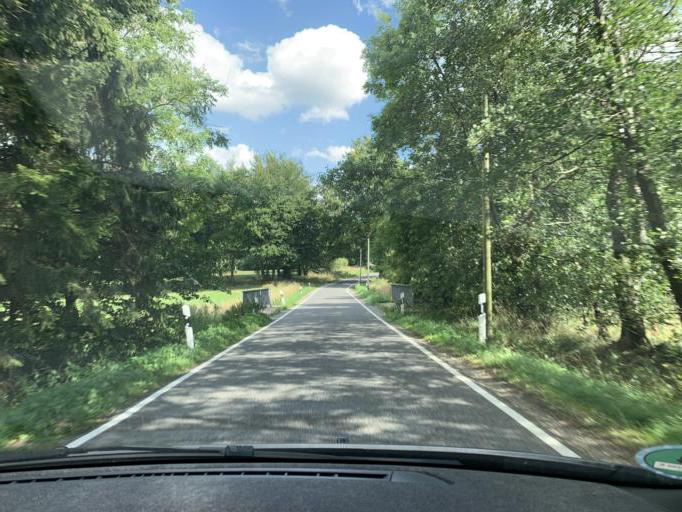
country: DE
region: North Rhine-Westphalia
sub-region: Regierungsbezirk Koln
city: Simmerath
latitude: 50.6038
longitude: 6.2663
